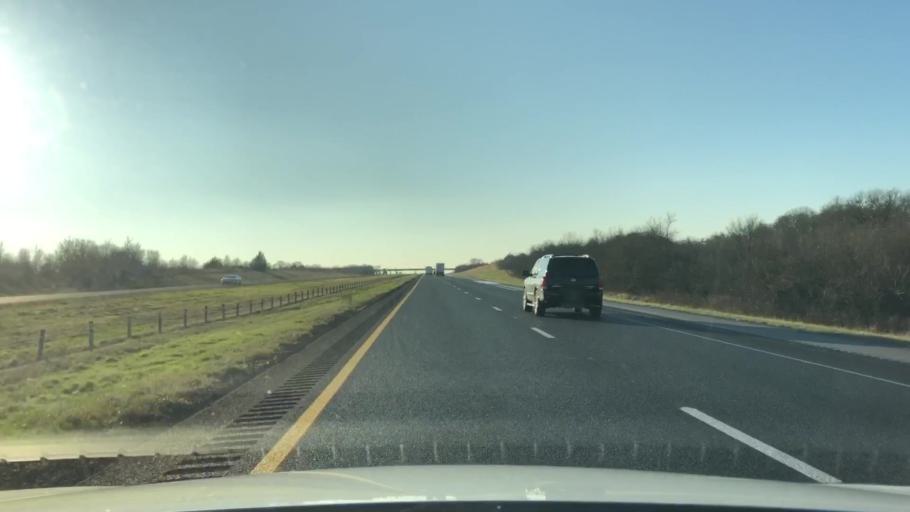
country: US
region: Texas
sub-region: Gonzales County
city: Waelder
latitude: 29.6677
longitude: -97.3236
